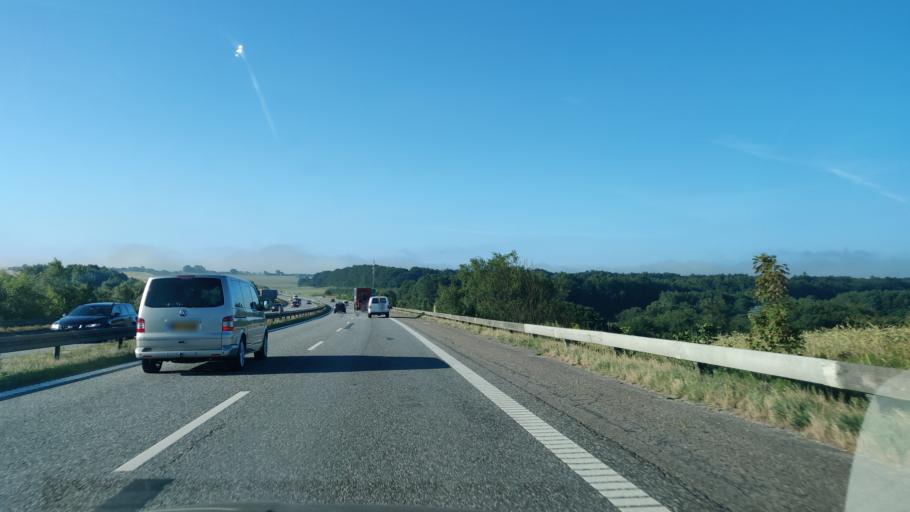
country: DK
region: North Denmark
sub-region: Mariagerfjord Kommune
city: Hobro
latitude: 56.6187
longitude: 9.7336
